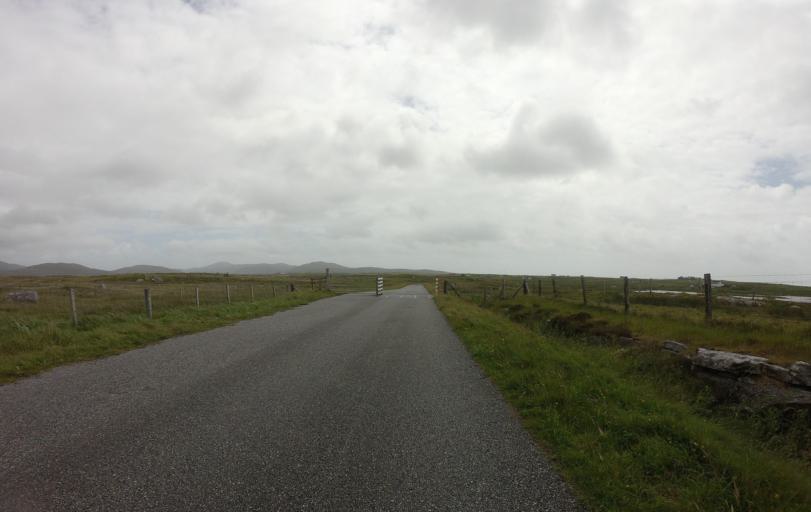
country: GB
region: Scotland
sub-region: Eilean Siar
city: Isle of South Uist
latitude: 57.2684
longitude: -7.3986
